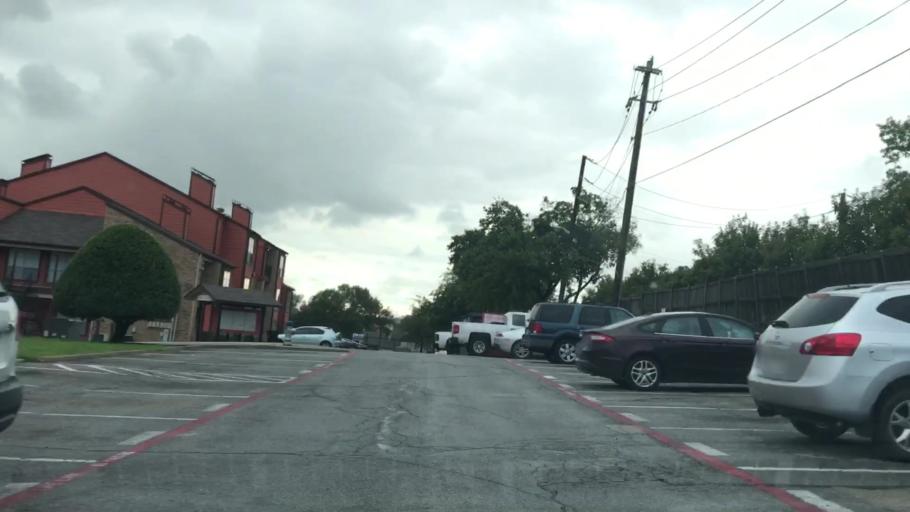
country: US
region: Texas
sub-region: Dallas County
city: Richardson
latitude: 32.8982
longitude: -96.7266
